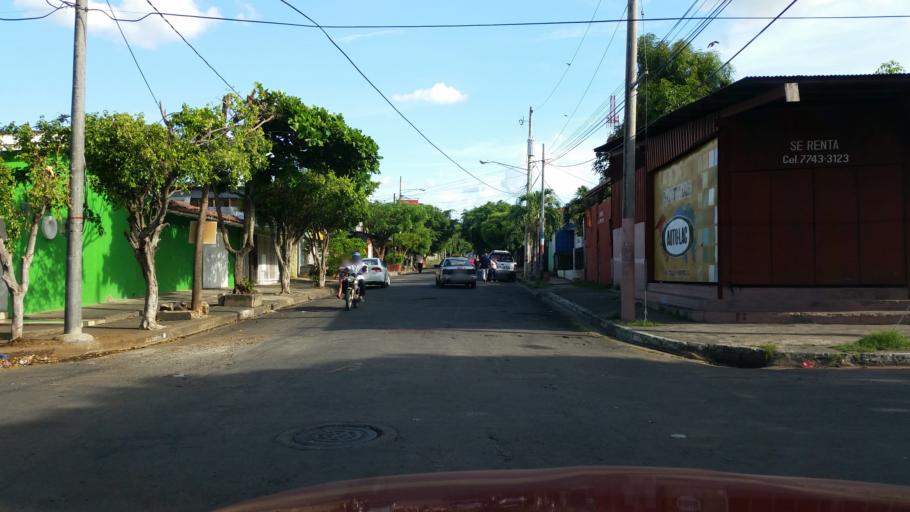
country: NI
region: Managua
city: Managua
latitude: 12.1449
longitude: -86.2813
